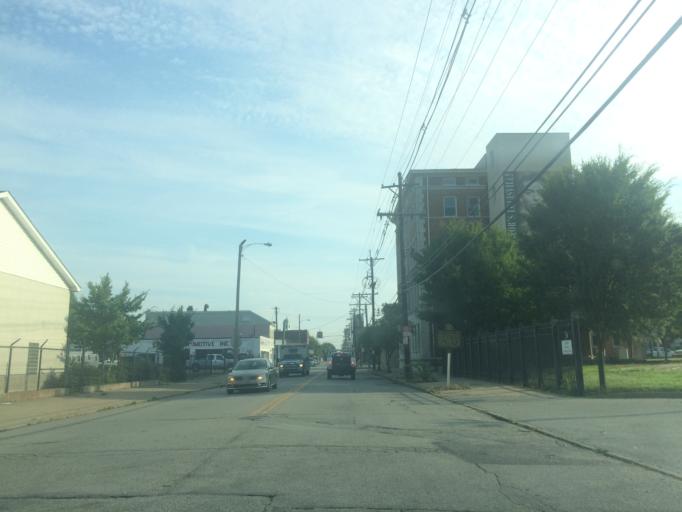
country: US
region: Kentucky
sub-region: Jefferson County
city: Louisville
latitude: 38.2301
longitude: -85.7421
